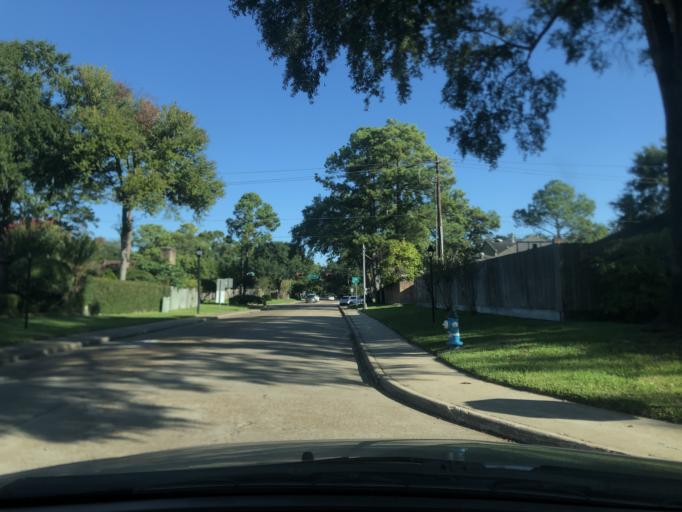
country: US
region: Texas
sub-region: Harris County
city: Bunker Hill Village
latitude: 29.7465
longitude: -95.5534
